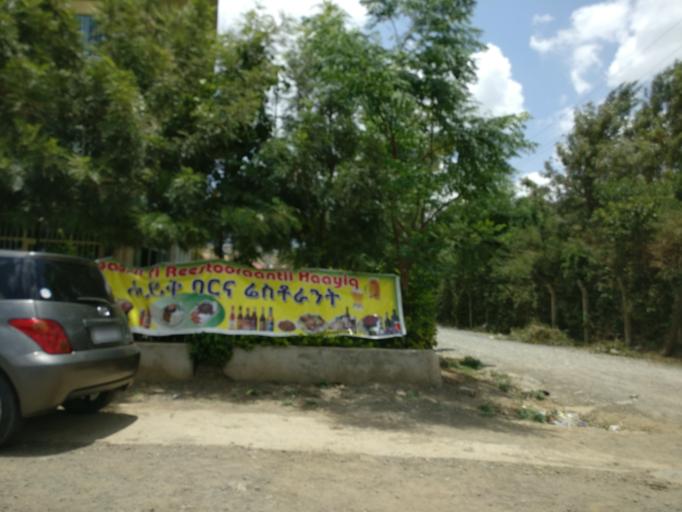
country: ET
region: Oromiya
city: Bishoftu
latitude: 8.7628
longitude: 38.9754
